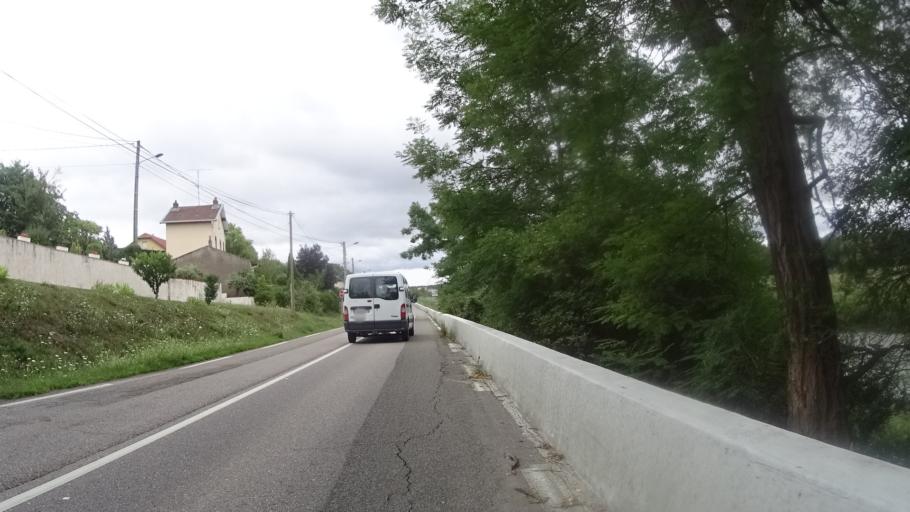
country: FR
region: Lorraine
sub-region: Departement de Meurthe-et-Moselle
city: Saint-Nicolas-de-Port
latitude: 48.6418
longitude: 6.2993
